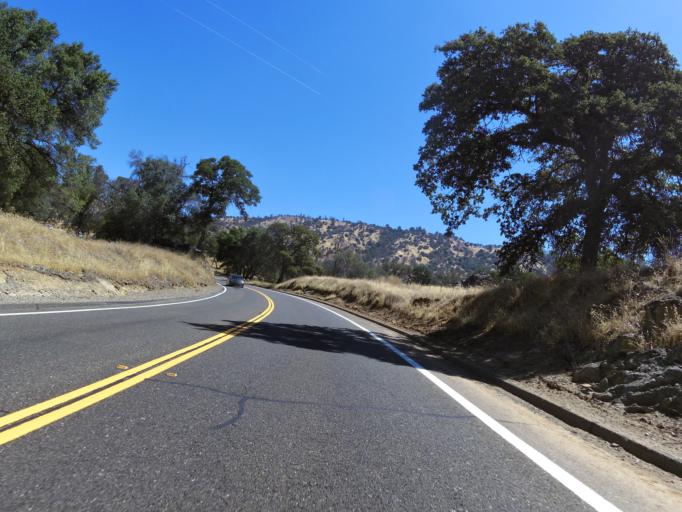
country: US
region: California
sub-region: Mariposa County
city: Mariposa
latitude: 37.4460
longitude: -120.0742
